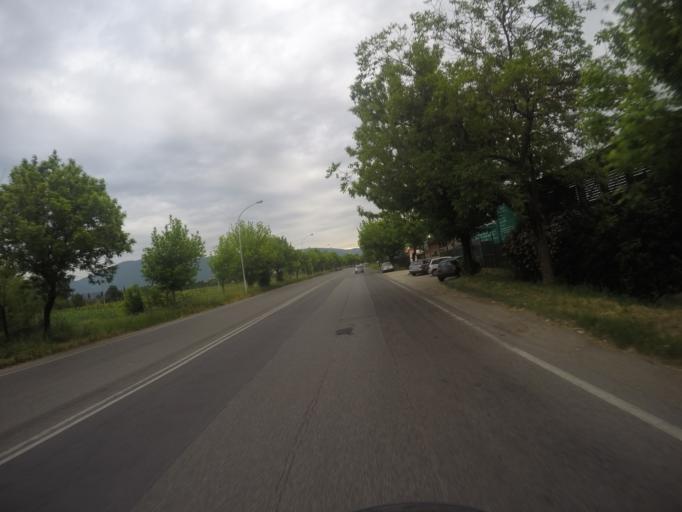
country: IT
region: Tuscany
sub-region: Provincia di Prato
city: Prato
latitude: 43.8954
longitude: 11.0720
